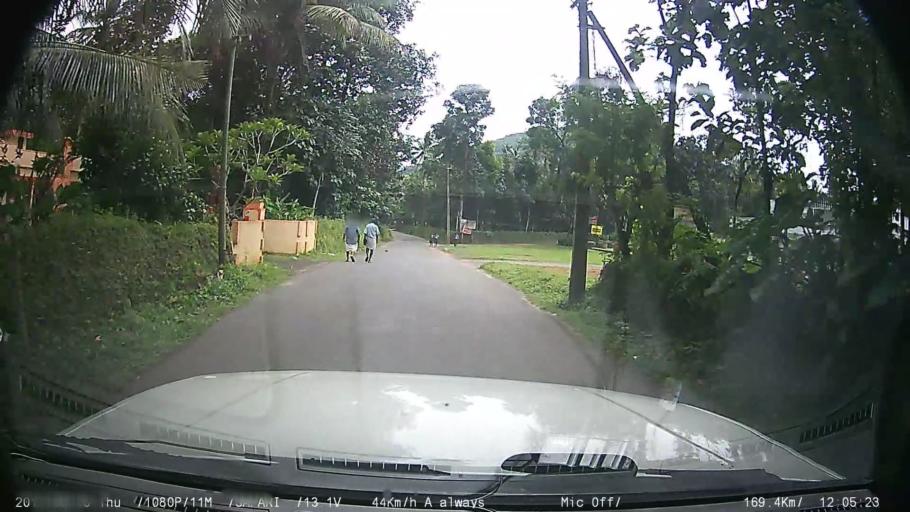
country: IN
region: Kerala
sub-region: Idukki
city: Kuttampuzha
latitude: 10.1050
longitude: 76.6831
